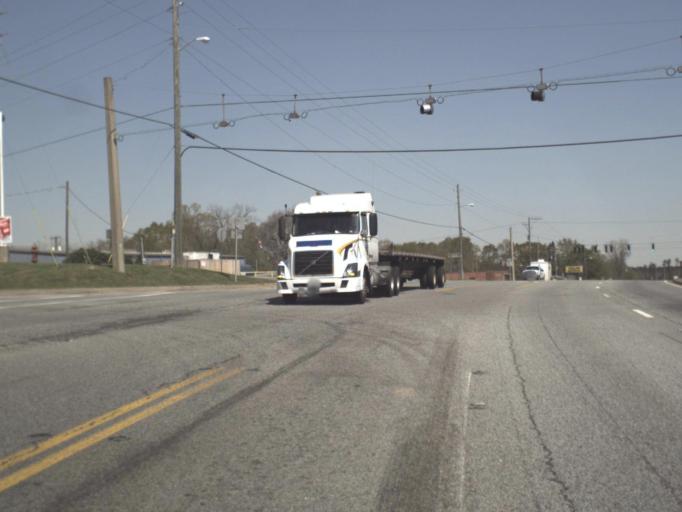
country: US
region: Florida
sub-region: Jackson County
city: Graceville
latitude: 30.9488
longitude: -85.4022
